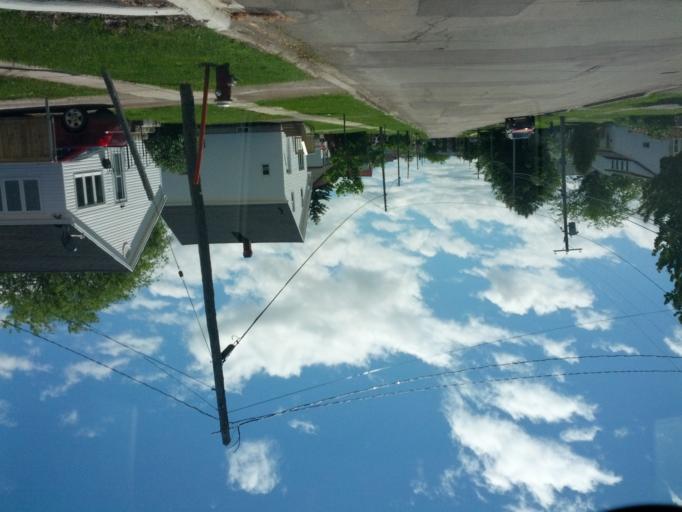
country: CA
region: New Brunswick
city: Moncton
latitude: 46.1150
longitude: -64.7744
